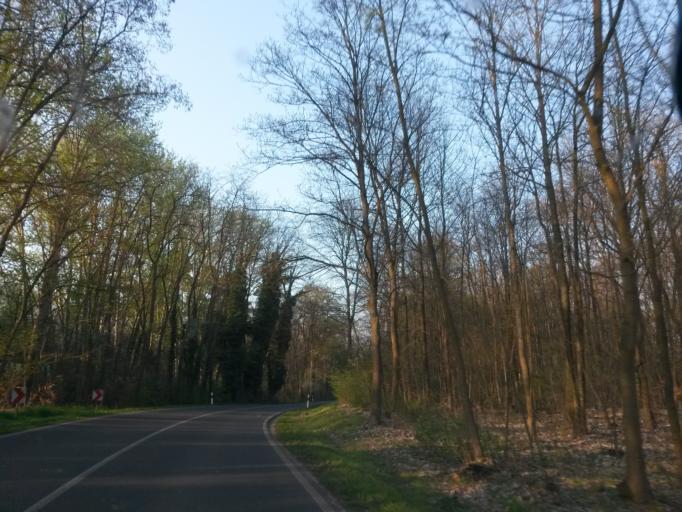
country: DE
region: Brandenburg
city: Rehfelde
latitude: 52.5400
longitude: 13.9360
